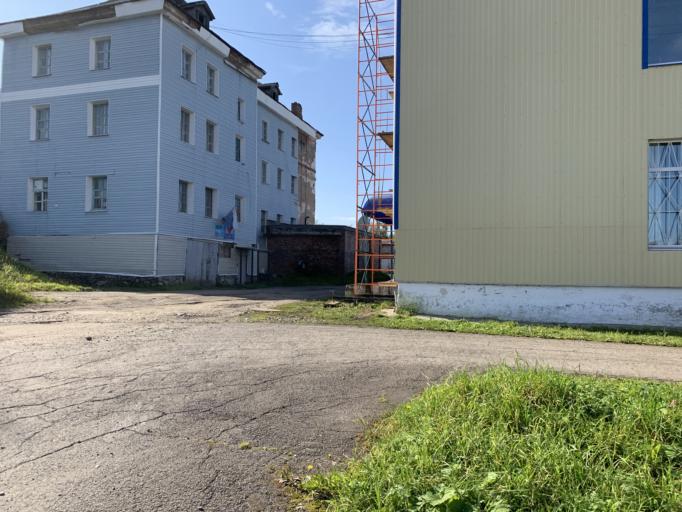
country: RU
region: Perm
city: Gubakha
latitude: 58.8429
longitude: 57.5559
